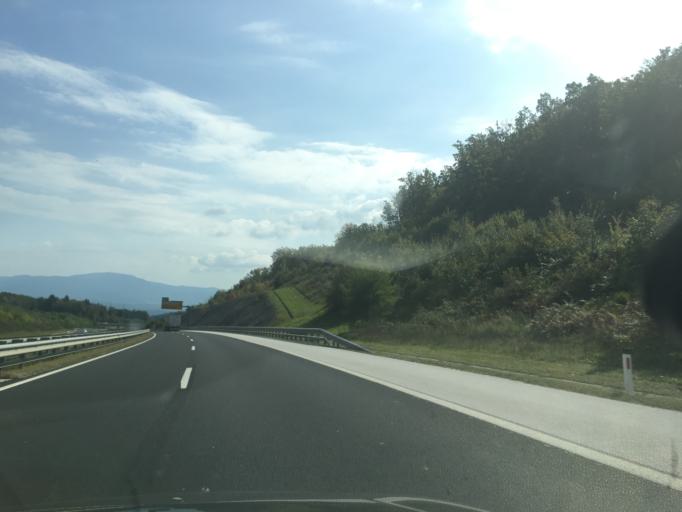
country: SI
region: Novo Mesto
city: Novo Mesto
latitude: 45.8458
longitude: 15.1497
